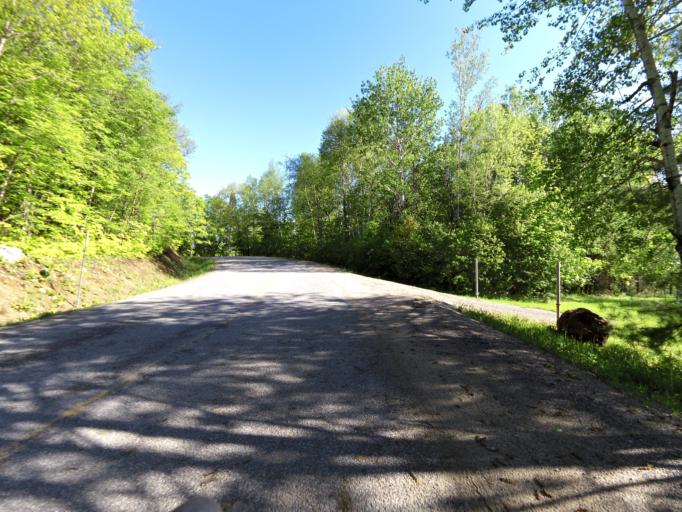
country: CA
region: Quebec
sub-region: Outaouais
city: Wakefield
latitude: 45.5996
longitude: -75.8580
